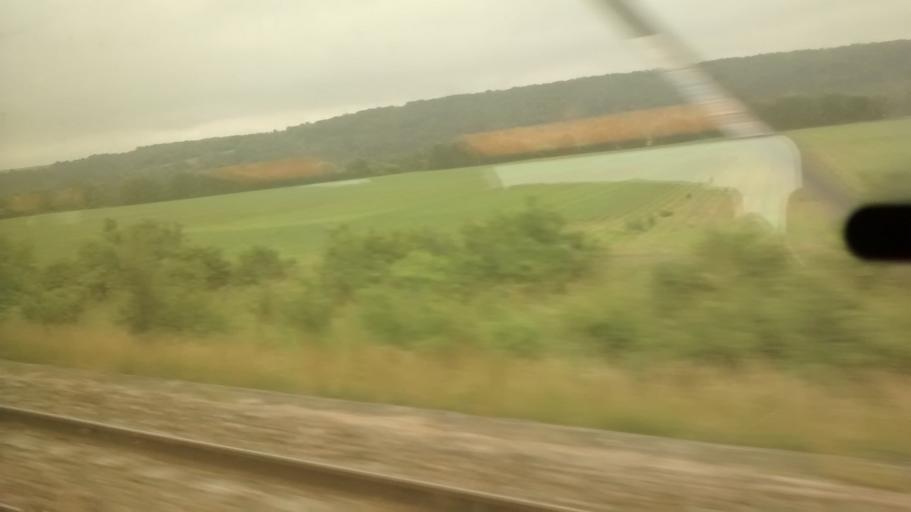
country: FR
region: Bourgogne
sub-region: Departement de l'Yonne
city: Malay-le-Grand
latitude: 48.1744
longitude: 3.3674
